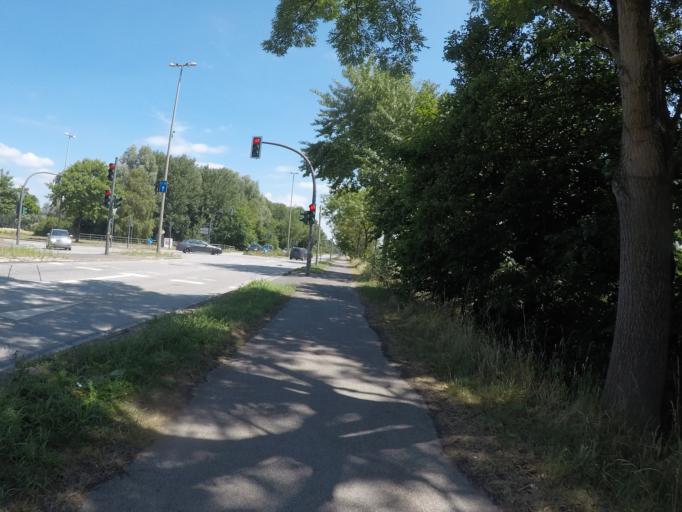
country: DE
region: Hamburg
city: Harburg
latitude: 53.4805
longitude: 10.0083
